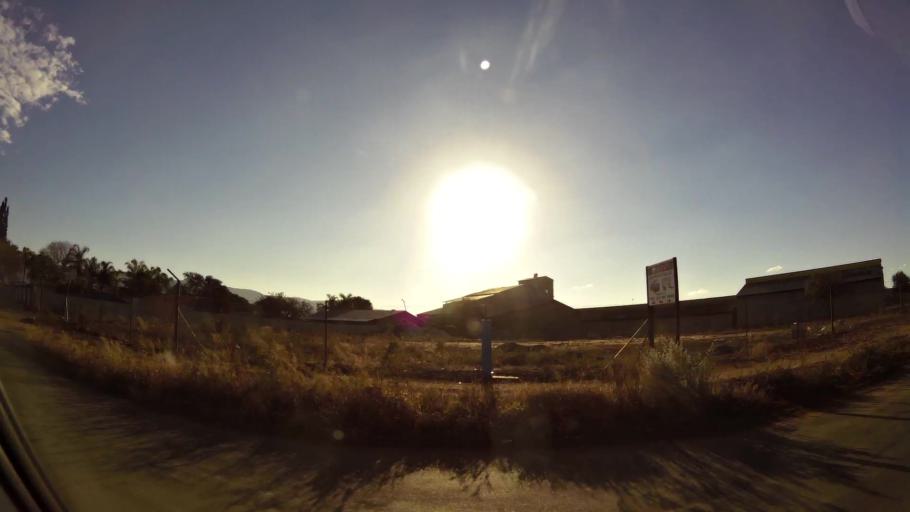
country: ZA
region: Limpopo
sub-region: Waterberg District Municipality
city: Mokopane
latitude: -24.1721
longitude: 29.0021
